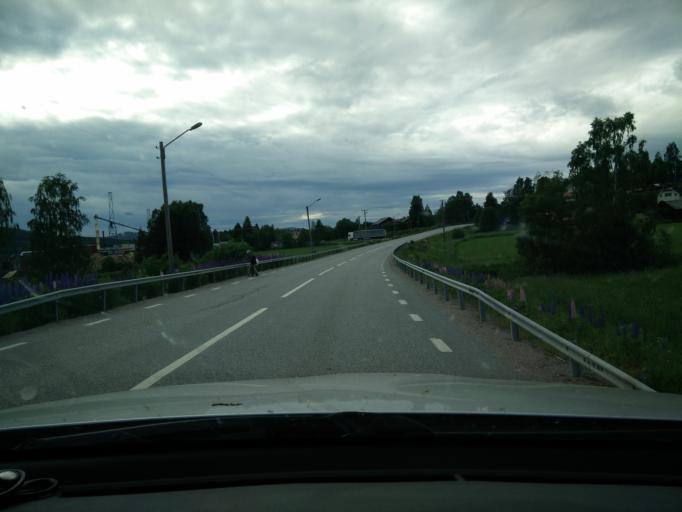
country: SE
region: Gaevleborg
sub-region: Hudiksvalls Kommun
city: Delsbo
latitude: 62.1001
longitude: 16.7287
